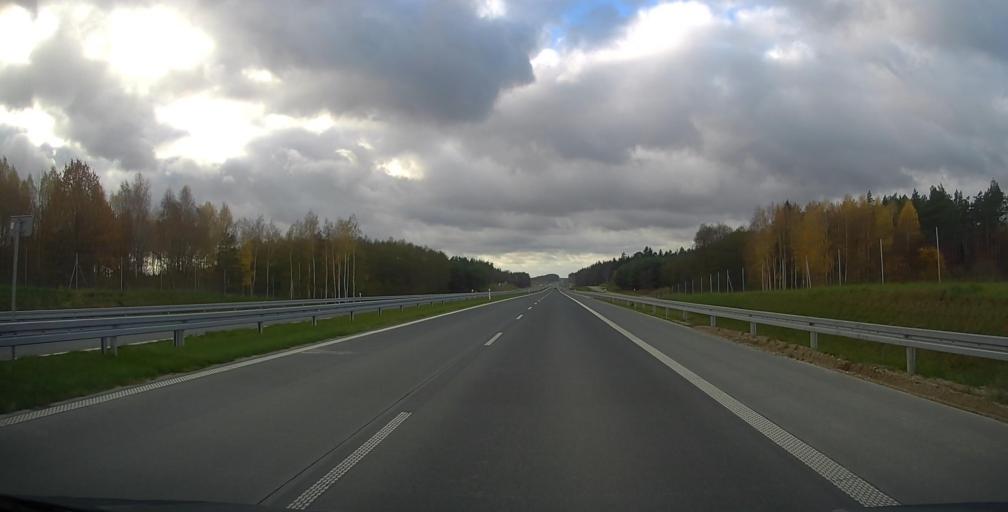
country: PL
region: Podlasie
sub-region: Powiat grajewski
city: Rajgrod
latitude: 53.8728
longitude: 22.6440
